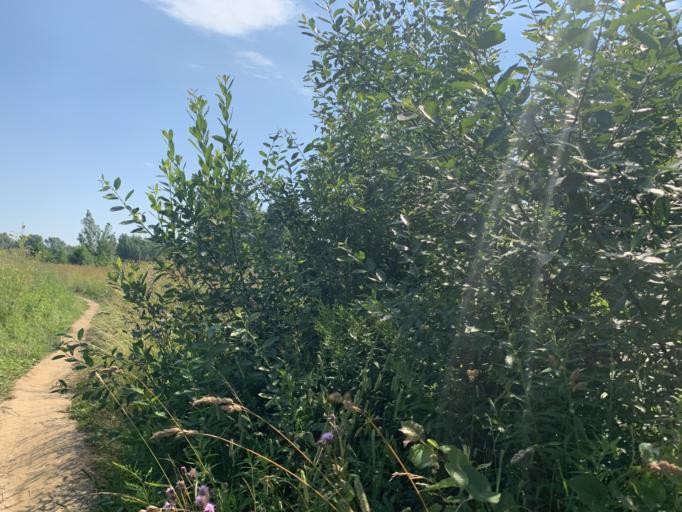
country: RU
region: Moskovskaya
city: Cherkizovo
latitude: 55.9738
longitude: 37.7941
